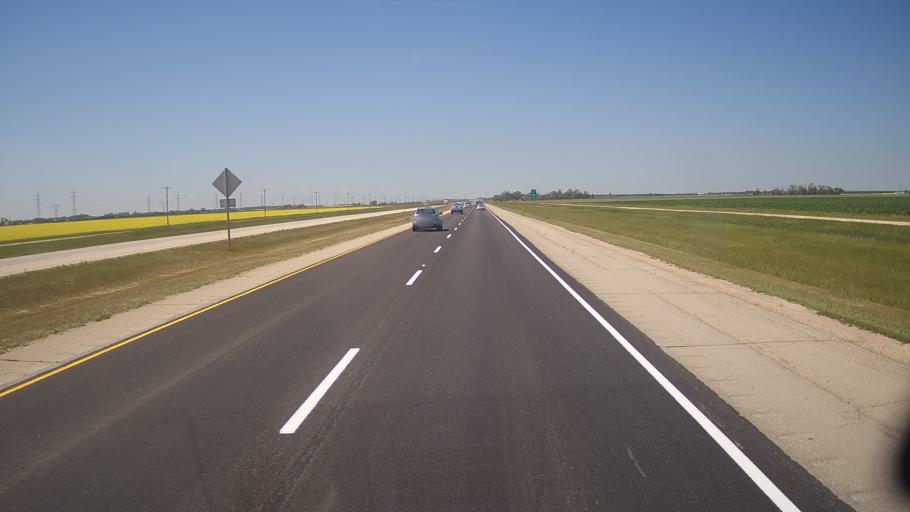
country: CA
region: Manitoba
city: Winnipeg
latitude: 49.9907
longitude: -97.1890
